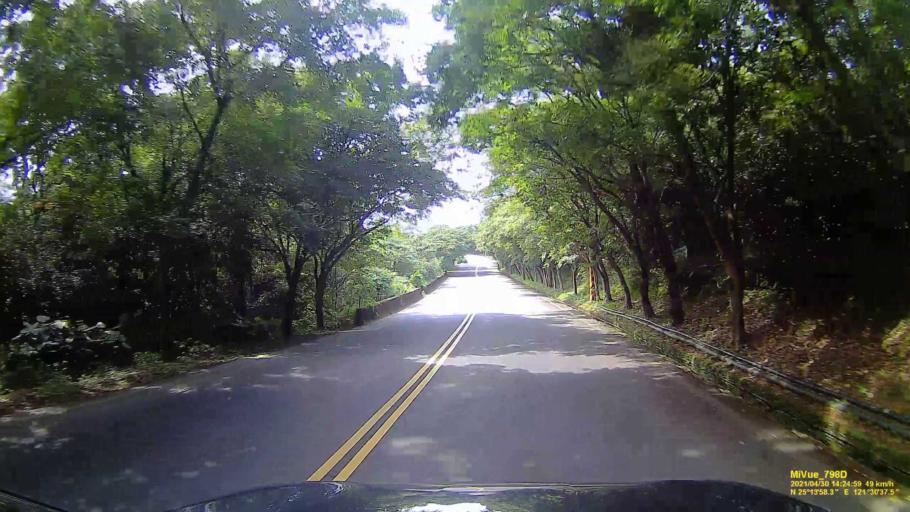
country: TW
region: Taipei
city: Taipei
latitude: 25.2332
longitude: 121.5102
